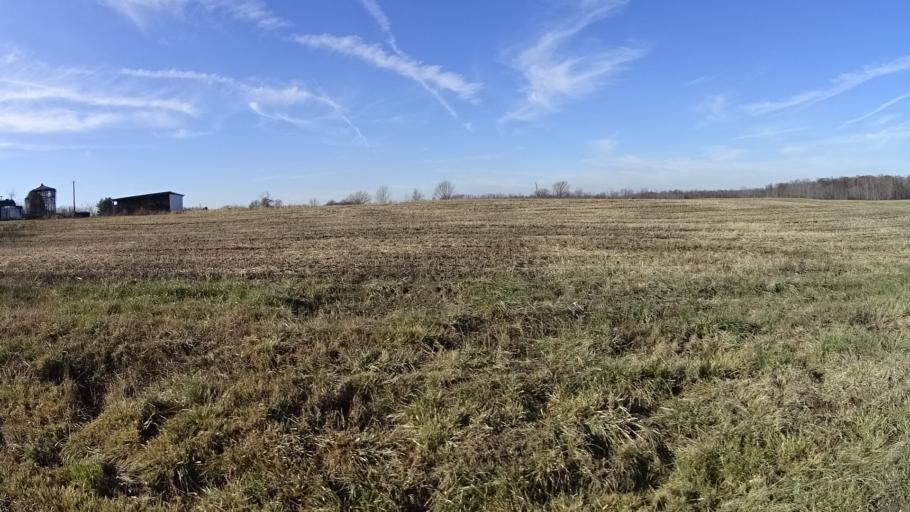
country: US
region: Ohio
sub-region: Huron County
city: New London
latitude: 41.0592
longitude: -82.2798
